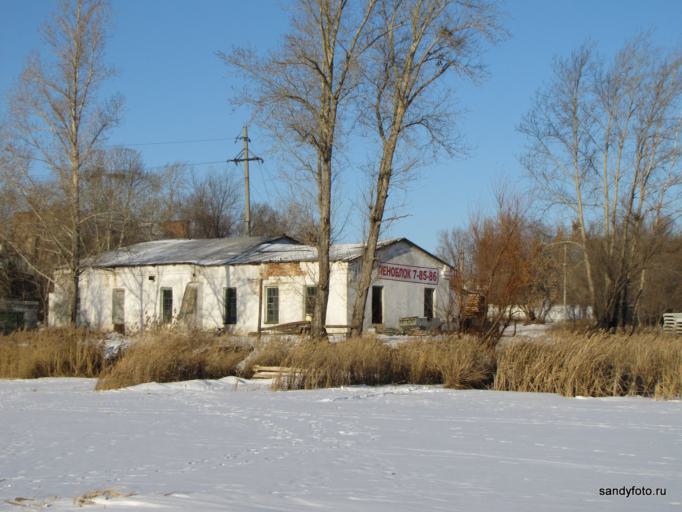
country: RU
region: Chelyabinsk
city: Troitsk
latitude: 54.0929
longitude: 61.5652
